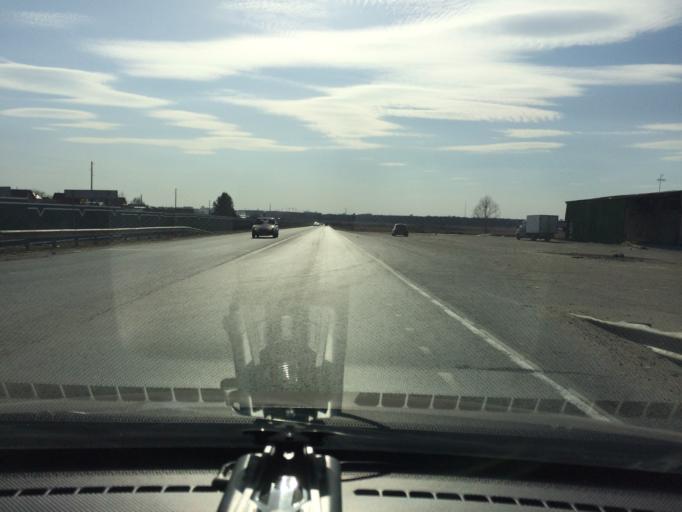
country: RU
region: Mariy-El
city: Yoshkar-Ola
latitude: 56.6593
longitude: 47.9714
